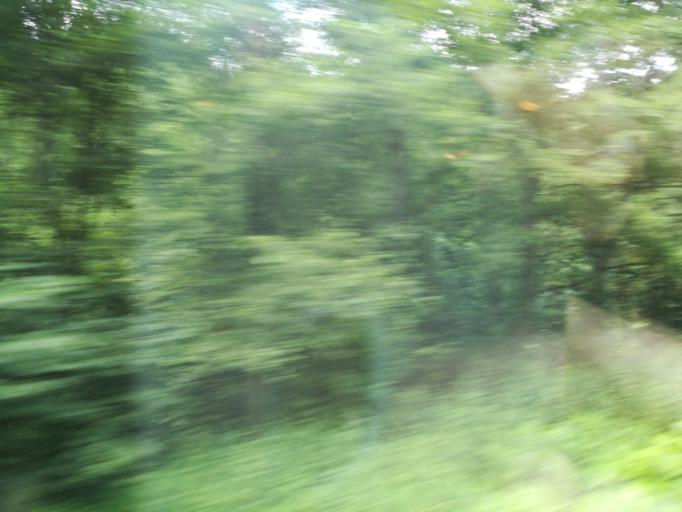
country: RO
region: Brasov
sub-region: Oras Predeal
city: Predeal
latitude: 45.5206
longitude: 25.6081
